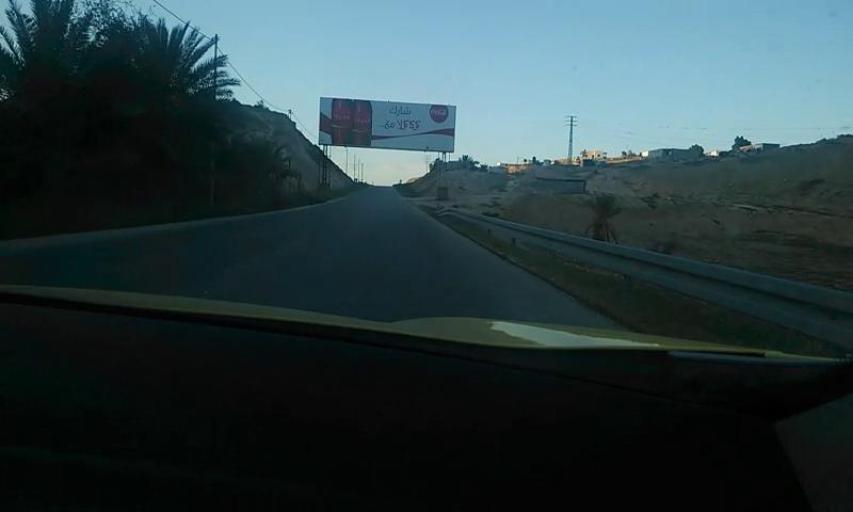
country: PS
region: West Bank
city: An Nuway`imah
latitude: 31.9011
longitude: 35.4268
